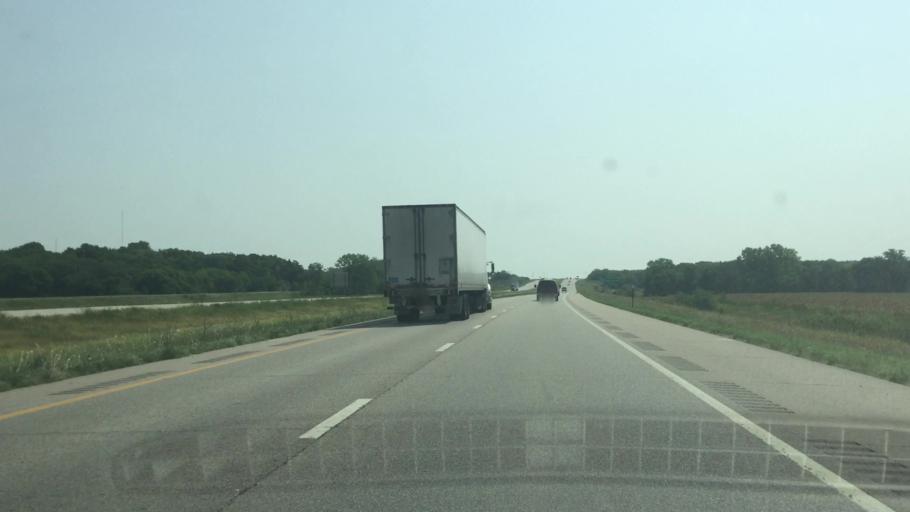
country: US
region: Kansas
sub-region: Lyon County
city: Emporia
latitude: 38.4110
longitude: -96.1106
